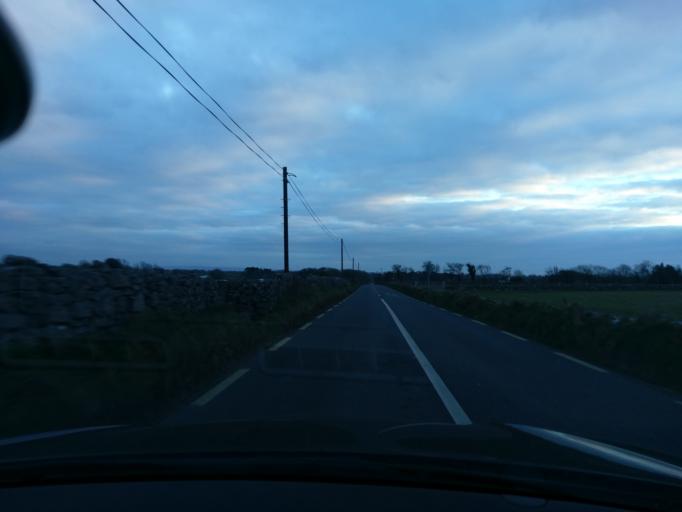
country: IE
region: Connaught
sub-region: County Galway
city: Athenry
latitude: 53.3614
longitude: -8.7758
